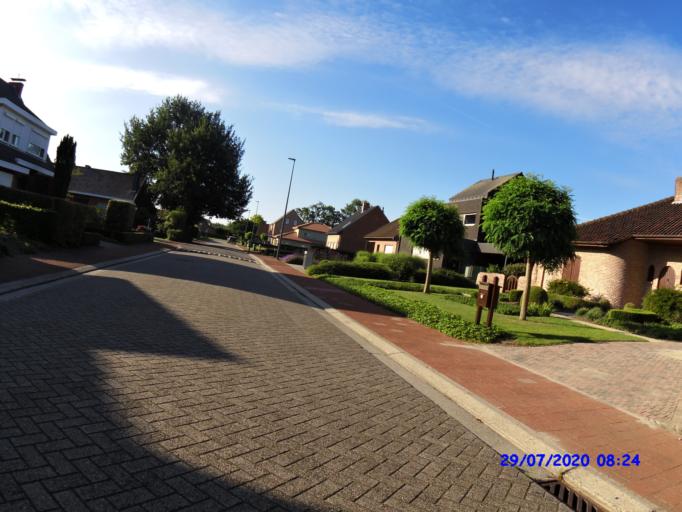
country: BE
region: Flanders
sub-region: Provincie Antwerpen
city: Brecht
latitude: 51.3420
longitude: 4.6496
